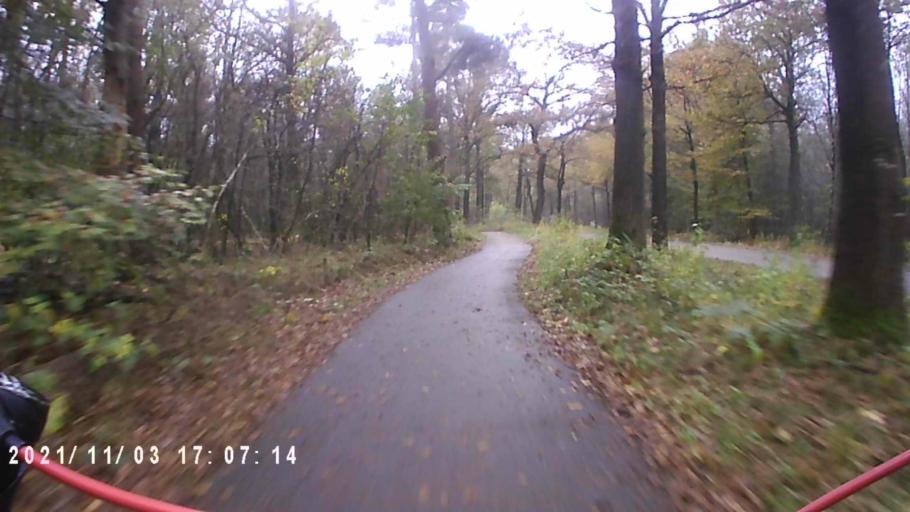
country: NL
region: Drenthe
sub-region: Gemeente Westerveld
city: Dwingeloo
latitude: 52.9509
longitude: 6.2996
